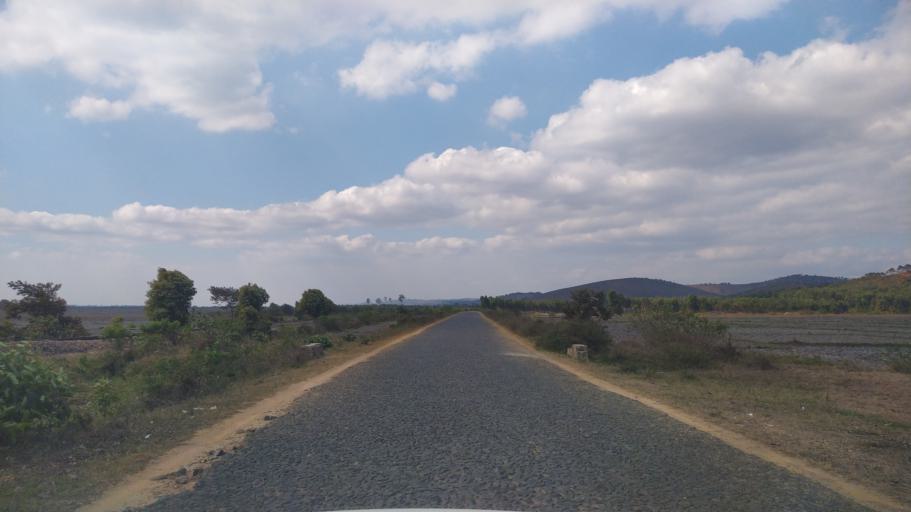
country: MG
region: Alaotra Mangoro
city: Moramanga
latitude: -18.7659
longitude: 48.2541
